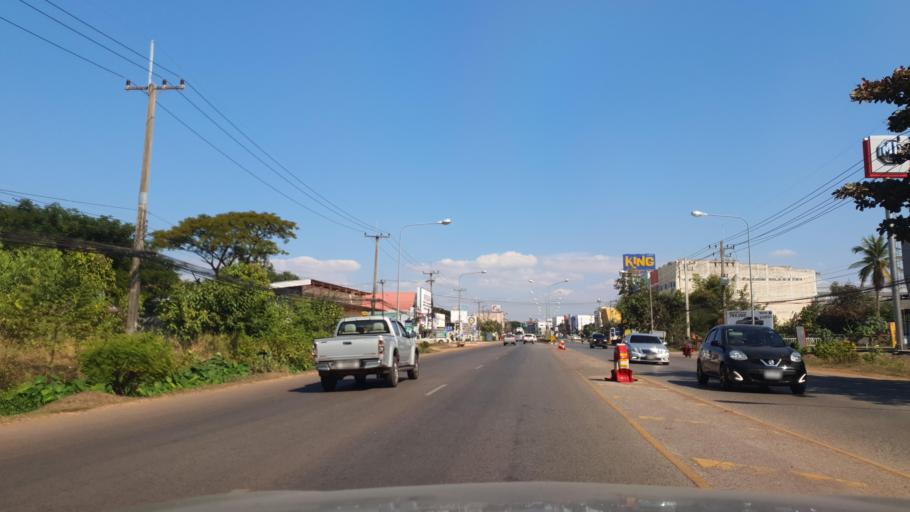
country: TH
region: Sakon Nakhon
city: Sakon Nakhon
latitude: 17.1470
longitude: 104.1272
